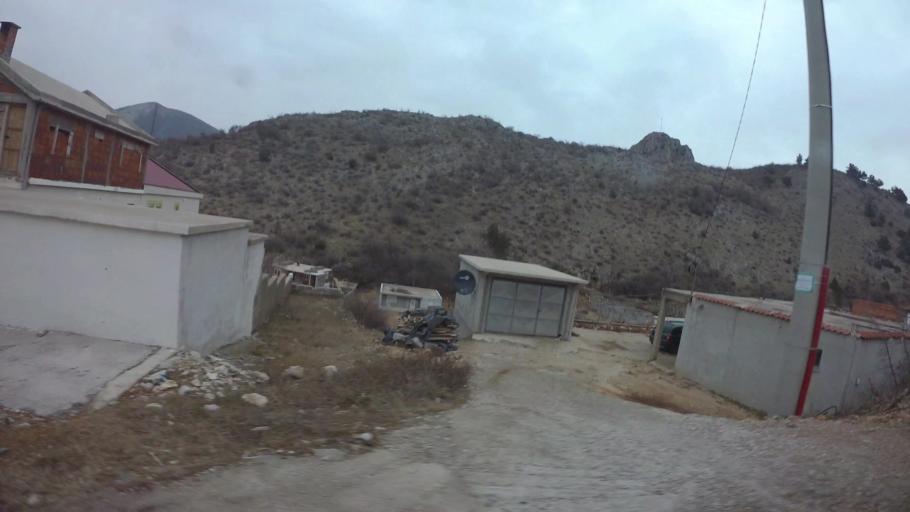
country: BA
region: Federation of Bosnia and Herzegovina
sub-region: Hercegovacko-Bosanski Kanton
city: Mostar
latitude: 43.3605
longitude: 17.8232
